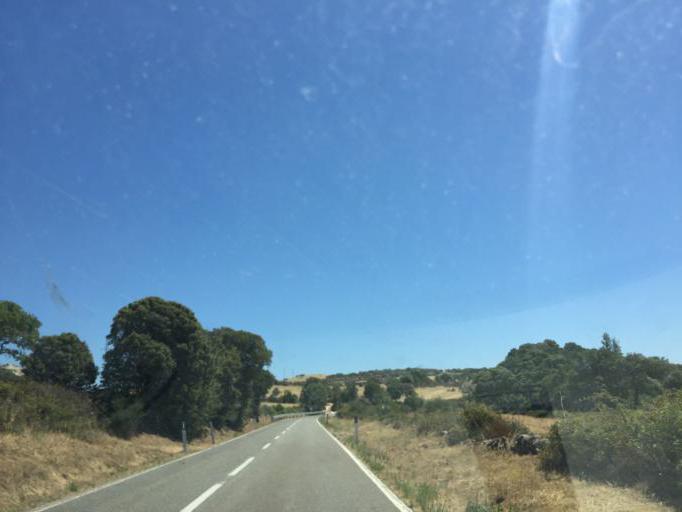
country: IT
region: Sardinia
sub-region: Provincia di Olbia-Tempio
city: Telti
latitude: 40.8981
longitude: 9.2857
